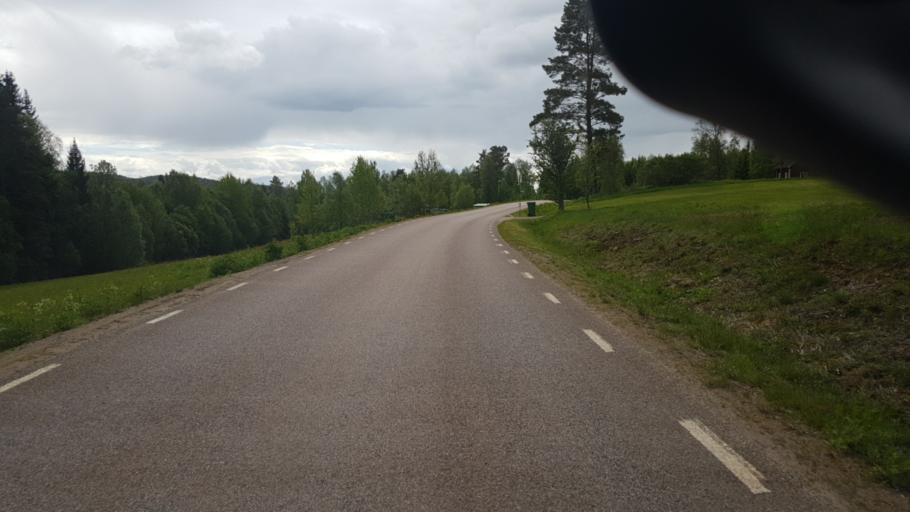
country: SE
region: Vaermland
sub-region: Arvika Kommun
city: Arvika
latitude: 59.7672
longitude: 12.8210
